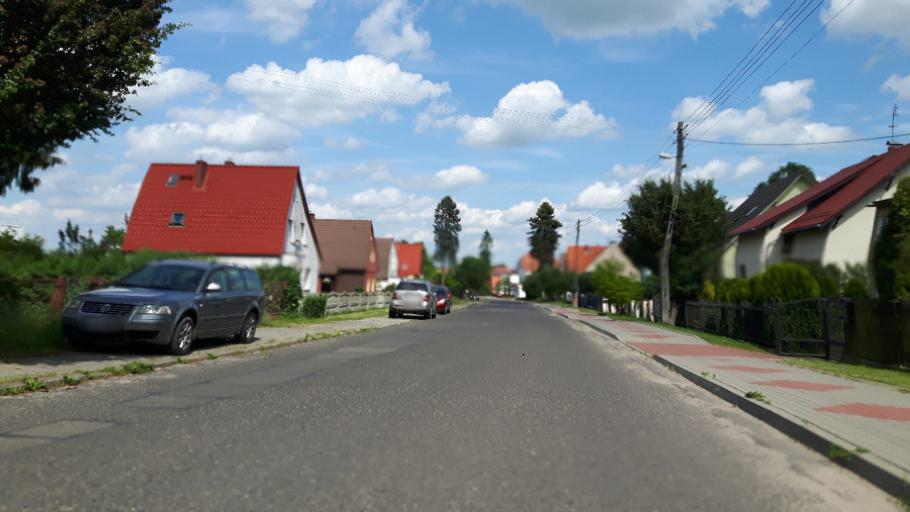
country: PL
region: West Pomeranian Voivodeship
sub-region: Powiat goleniowski
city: Nowogard
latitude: 53.6705
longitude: 15.0996
